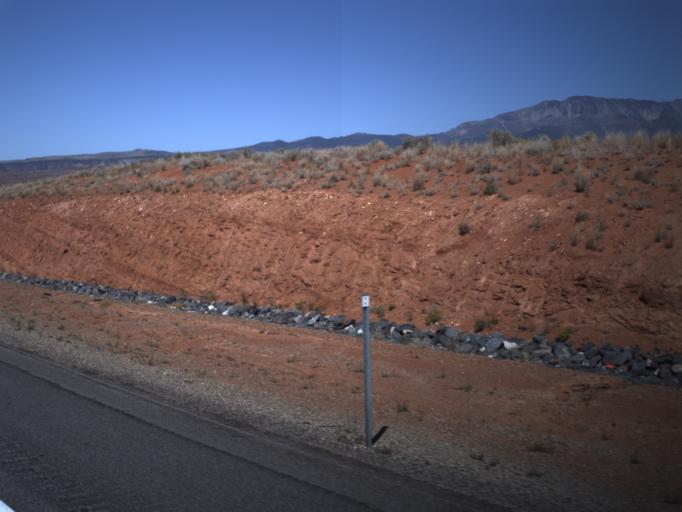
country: US
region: Utah
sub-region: Washington County
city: Washington
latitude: 37.1105
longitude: -113.4205
